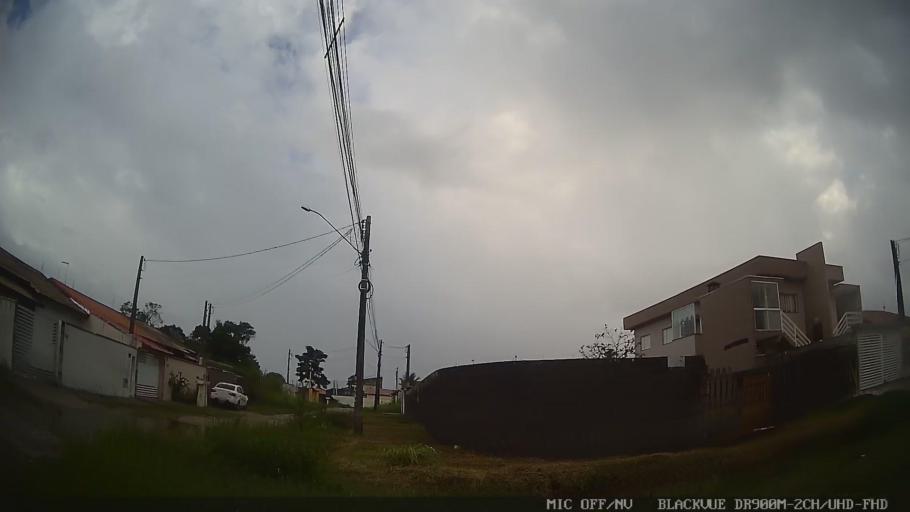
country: BR
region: Sao Paulo
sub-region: Itanhaem
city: Itanhaem
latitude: -24.2129
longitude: -46.8600
